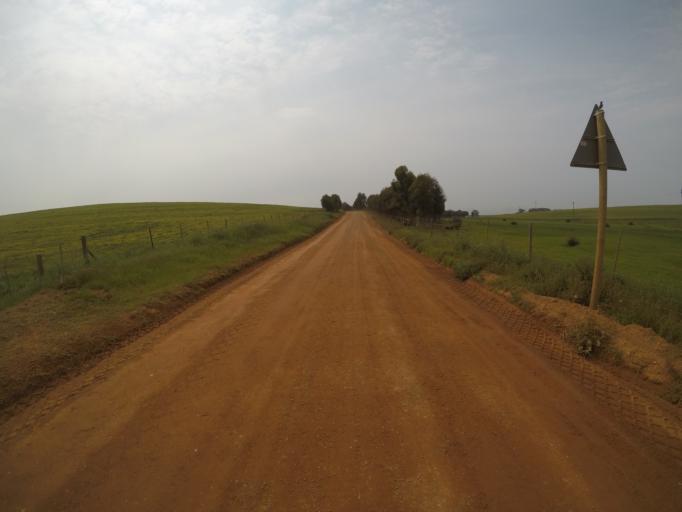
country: ZA
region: Western Cape
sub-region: City of Cape Town
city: Kraaifontein
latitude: -33.7254
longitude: 18.6525
